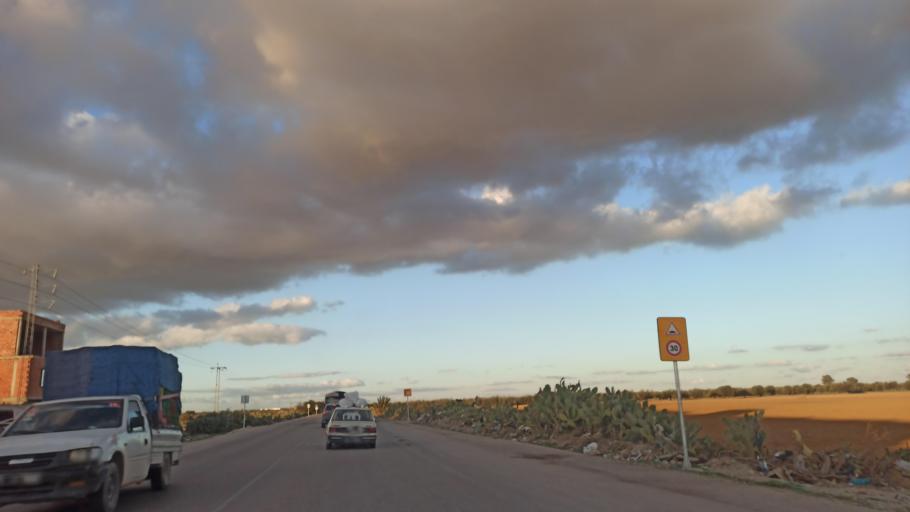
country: TN
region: Susah
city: Sidi Bou Ali
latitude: 36.0122
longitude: 10.3183
